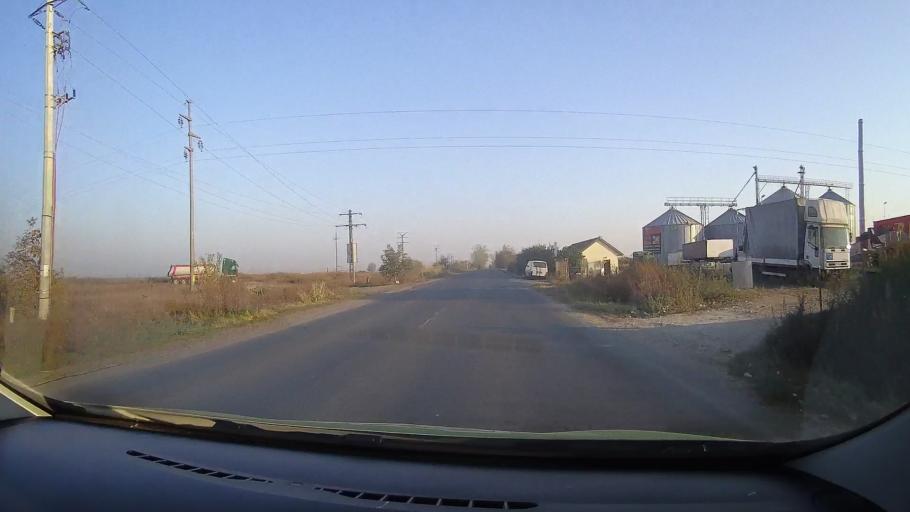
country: RO
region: Arad
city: Arad
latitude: 46.2192
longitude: 21.3205
